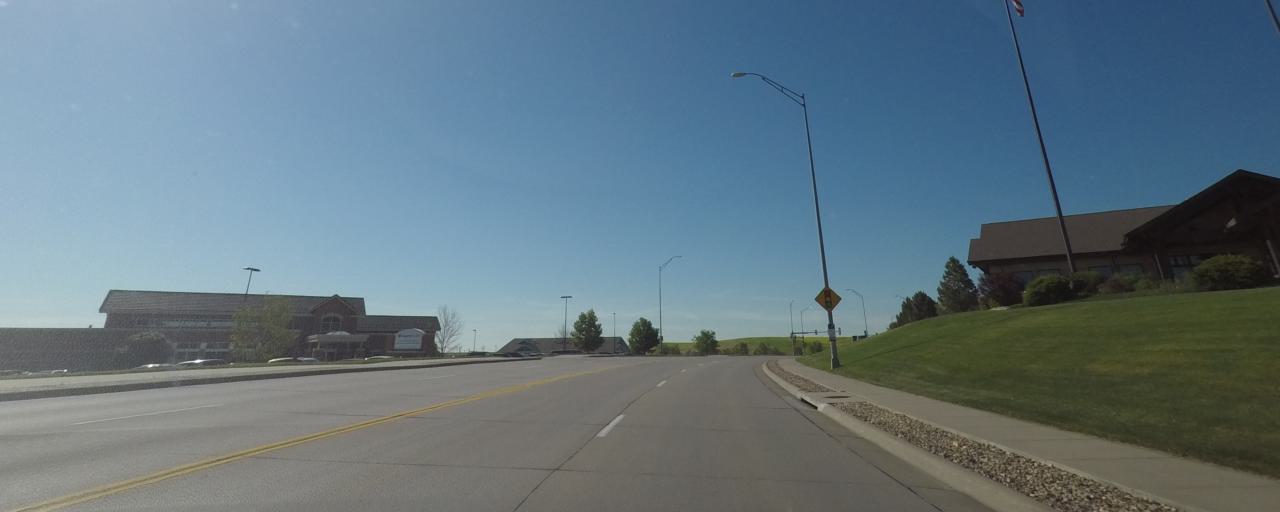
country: US
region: South Dakota
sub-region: Pennington County
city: Rapid City
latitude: 44.0447
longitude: -103.2199
